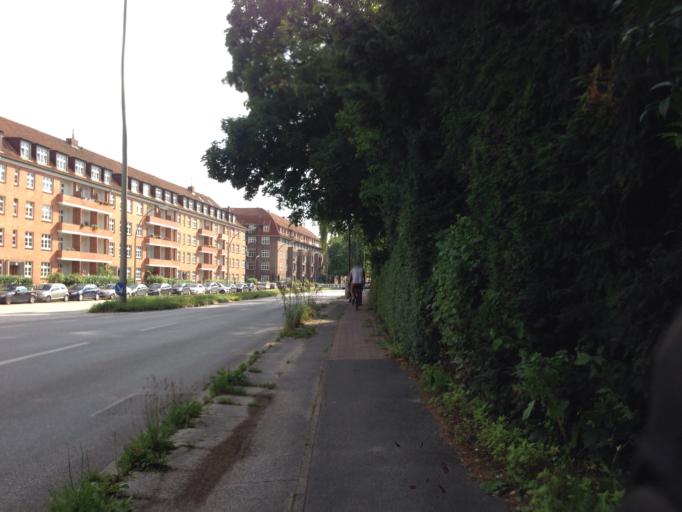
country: DE
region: Hamburg
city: Hamburg-Nord
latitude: 53.5897
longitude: 9.9821
